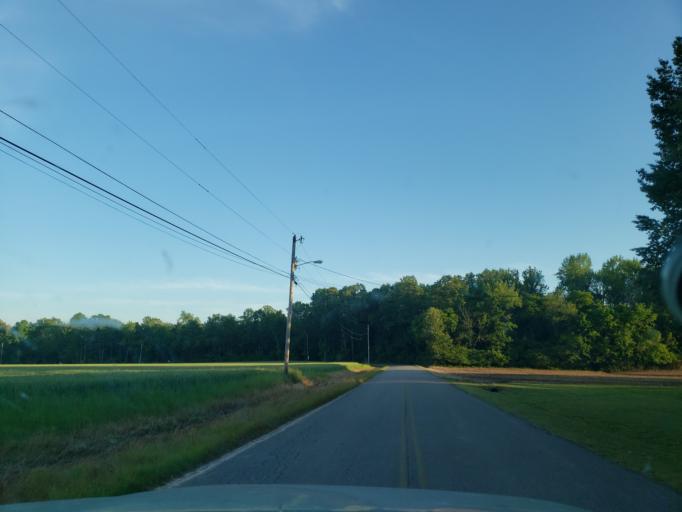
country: US
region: Alabama
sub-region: Madison County
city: Hazel Green
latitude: 34.9411
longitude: -86.5270
